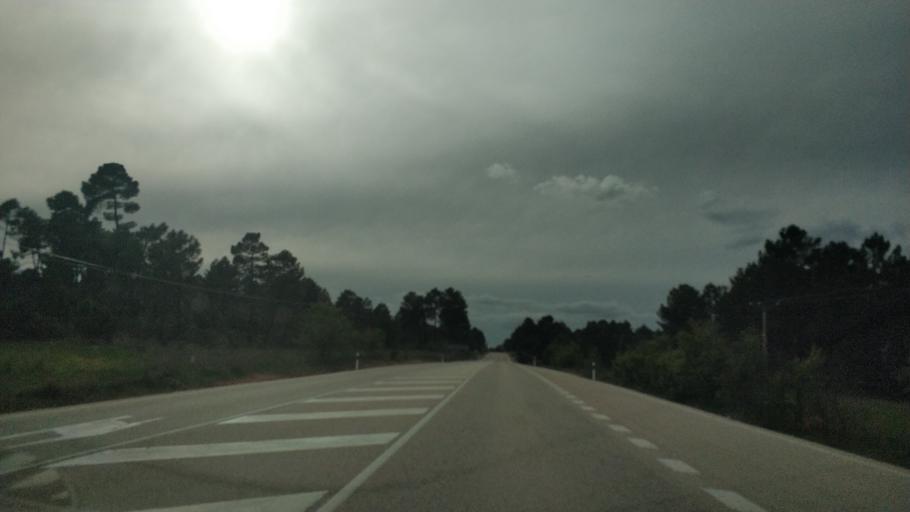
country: ES
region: Castille and Leon
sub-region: Provincia de Soria
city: Valdenebro
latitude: 41.5606
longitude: -2.9748
